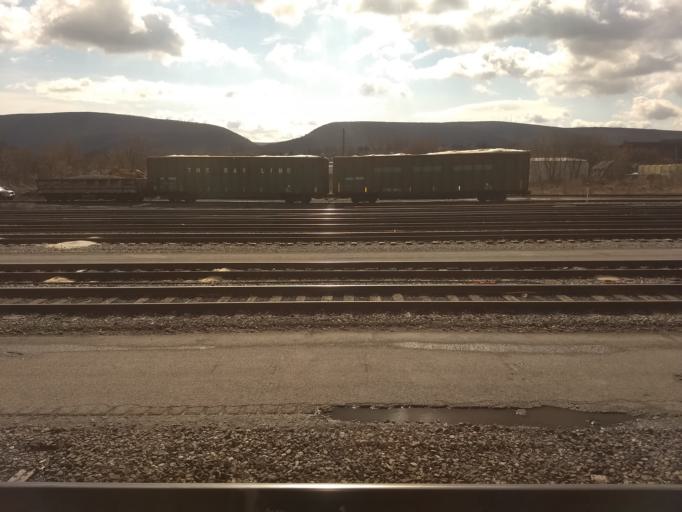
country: US
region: Pennsylvania
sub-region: Blair County
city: Altoona
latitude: 40.5225
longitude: -78.3917
